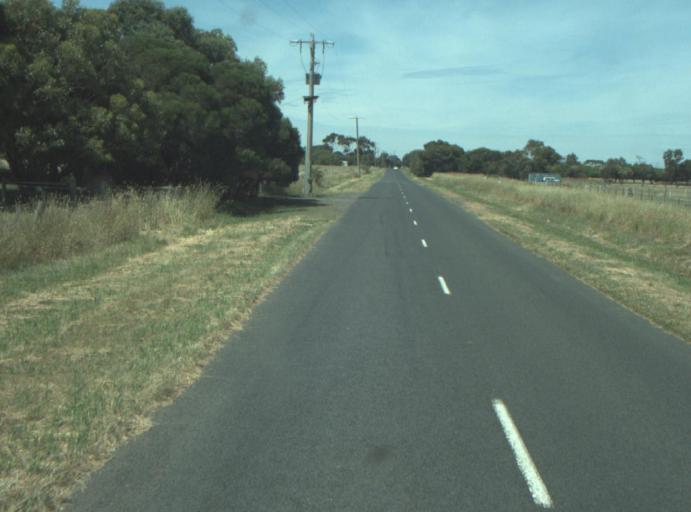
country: AU
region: Victoria
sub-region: Greater Geelong
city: Leopold
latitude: -38.1672
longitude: 144.4549
